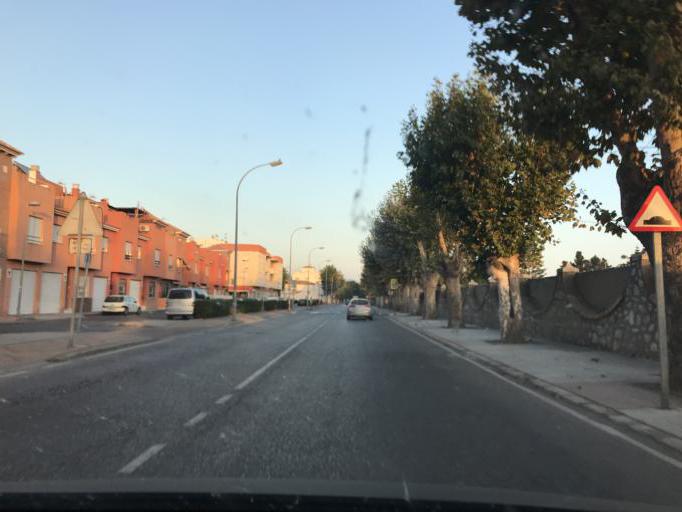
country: ES
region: Andalusia
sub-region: Provincia de Granada
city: El Varadero
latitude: 36.7256
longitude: -3.5303
